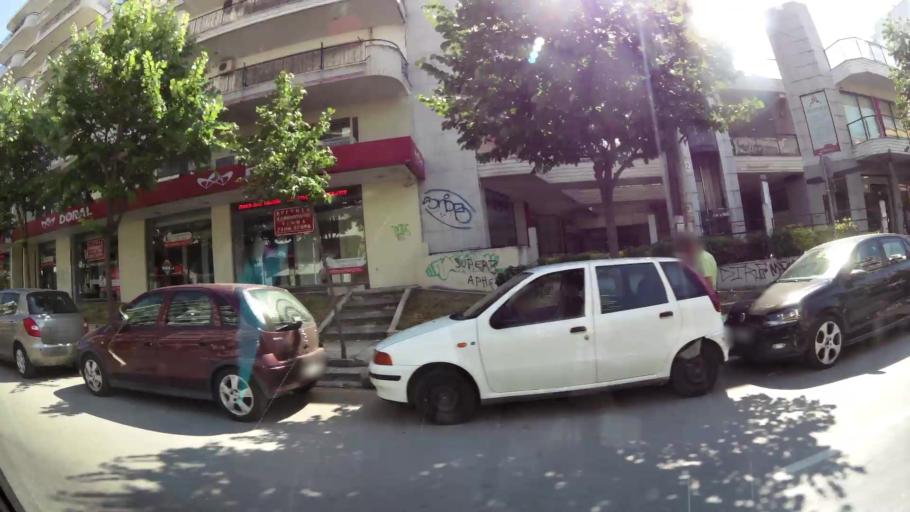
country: GR
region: Central Macedonia
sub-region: Nomos Thessalonikis
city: Kalamaria
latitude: 40.5846
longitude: 22.9578
